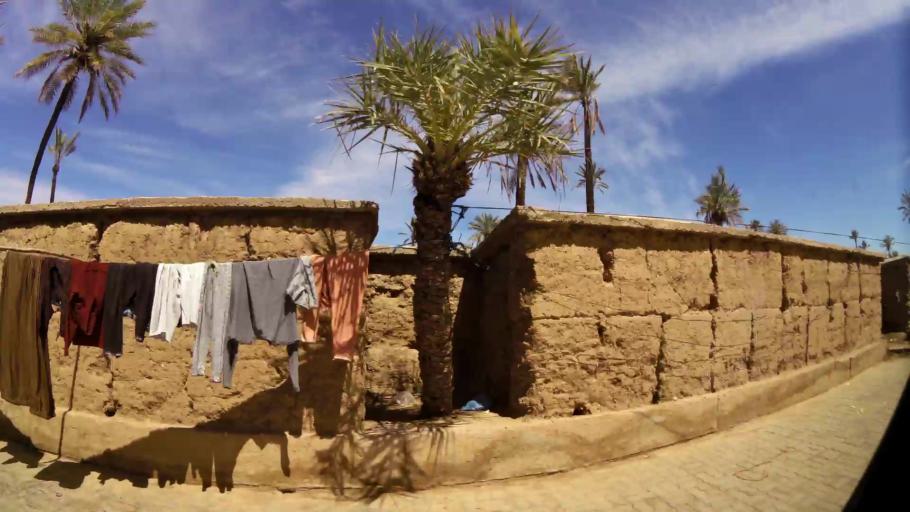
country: MA
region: Marrakech-Tensift-Al Haouz
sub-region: Marrakech
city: Marrakesh
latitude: 31.6665
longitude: -7.9864
